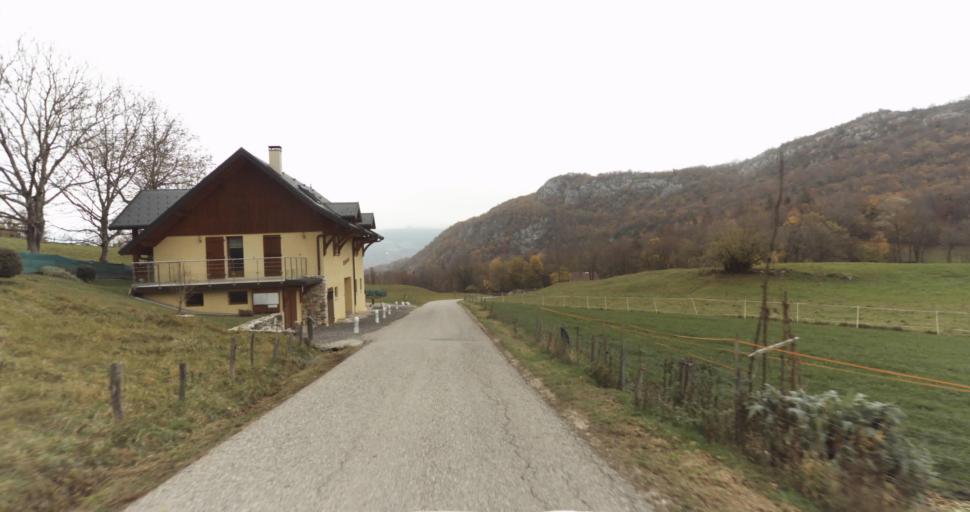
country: FR
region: Rhone-Alpes
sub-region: Departement de la Haute-Savoie
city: Saint-Jorioz
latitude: 45.8120
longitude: 6.1930
